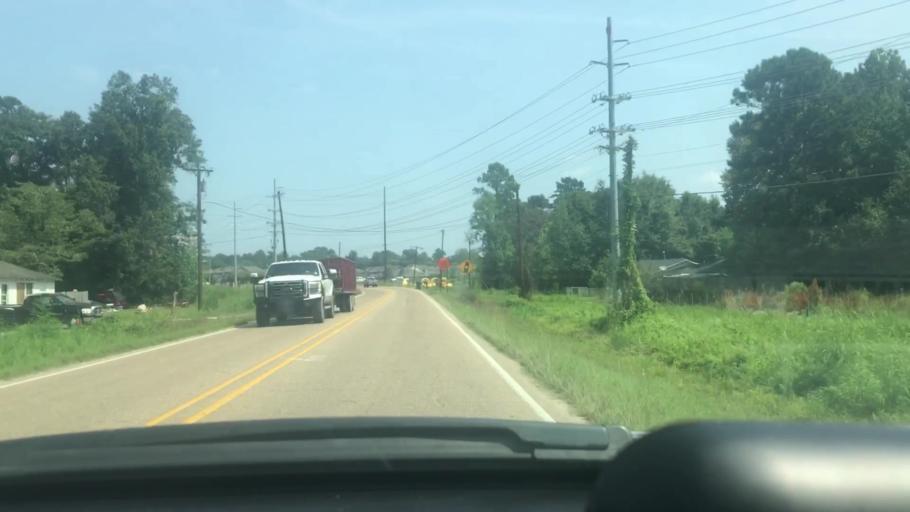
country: US
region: Louisiana
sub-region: Livingston Parish
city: Denham Springs
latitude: 30.4807
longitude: -90.9180
